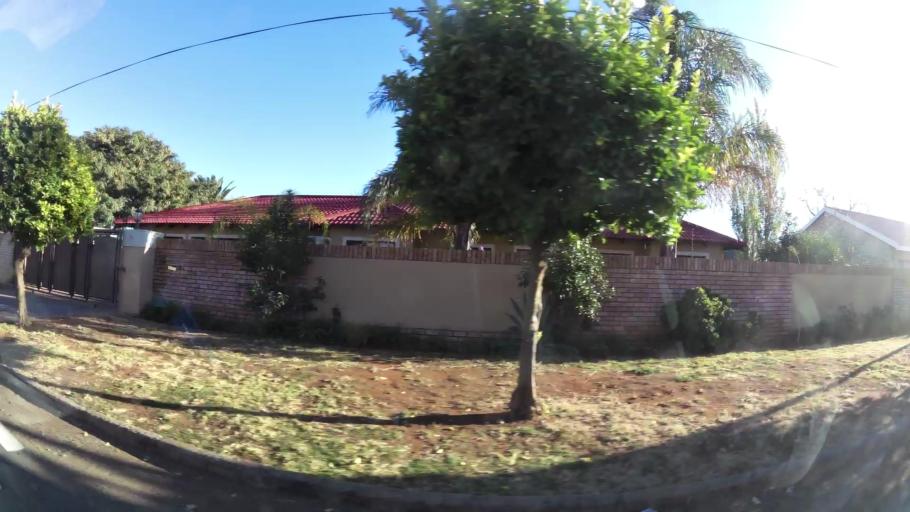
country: ZA
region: Northern Cape
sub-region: Frances Baard District Municipality
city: Kimberley
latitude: -28.7490
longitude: 24.7348
